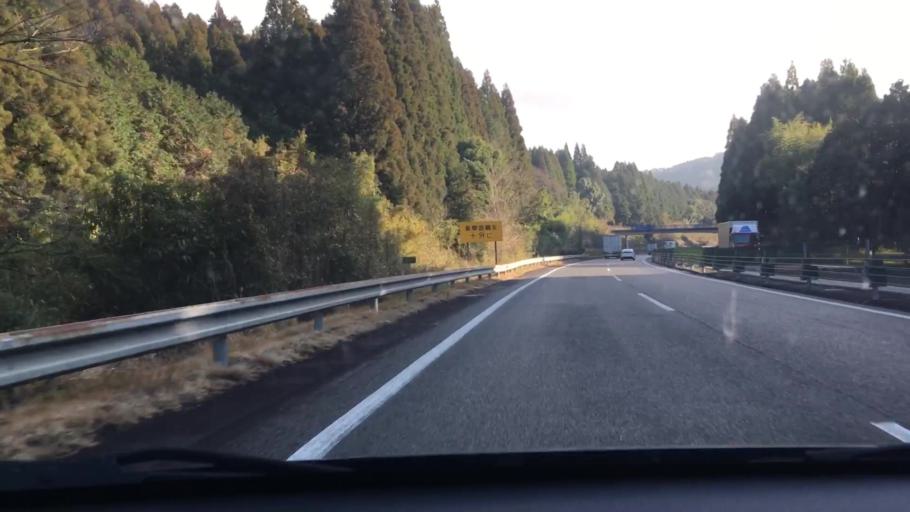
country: JP
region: Kagoshima
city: Okuchi-shinohara
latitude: 32.0000
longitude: 130.7582
